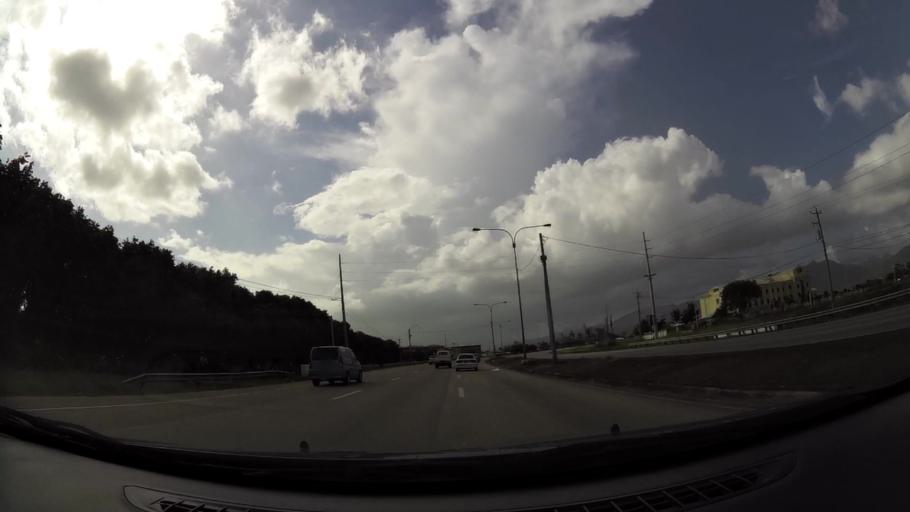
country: TT
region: Tunapuna/Piarco
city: Arouca
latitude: 10.6171
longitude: -61.3489
